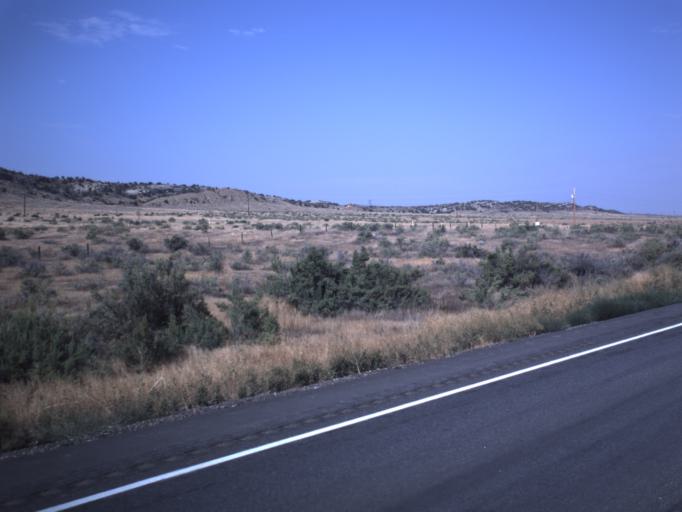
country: US
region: Utah
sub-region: Uintah County
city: Naples
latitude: 40.2956
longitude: -109.1814
